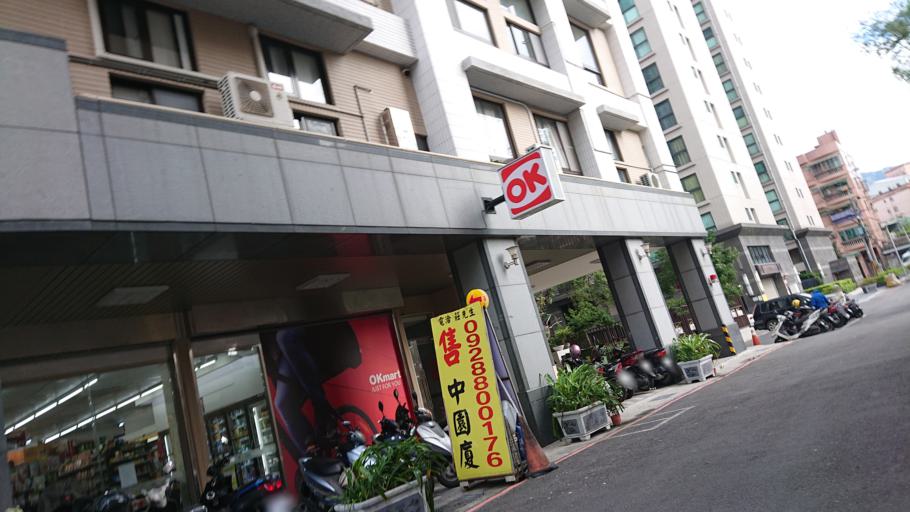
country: TW
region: Taiwan
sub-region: Taoyuan
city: Taoyuan
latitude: 24.9274
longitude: 121.3667
